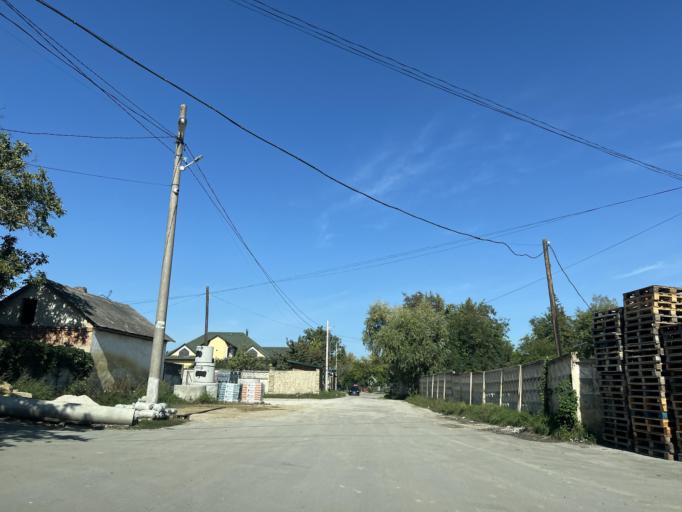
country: RO
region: Iasi
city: Ungheni-Prut
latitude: 47.1939
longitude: 27.7979
